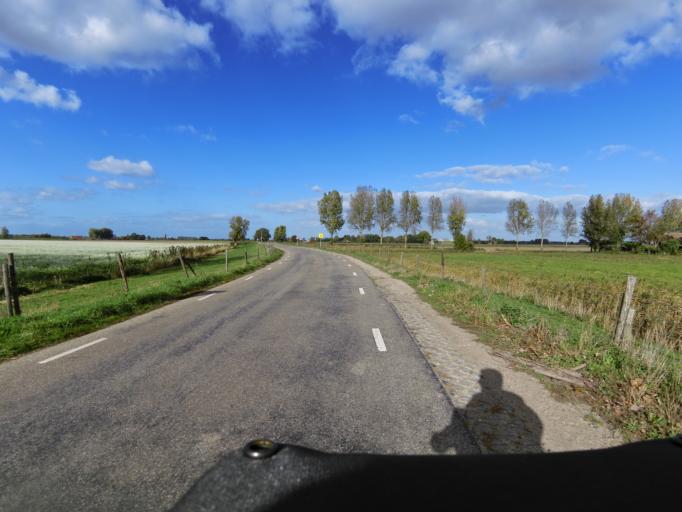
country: NL
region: North Brabant
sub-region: Gemeente Bergen op Zoom
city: Lepelstraat
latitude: 51.5680
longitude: 4.2676
